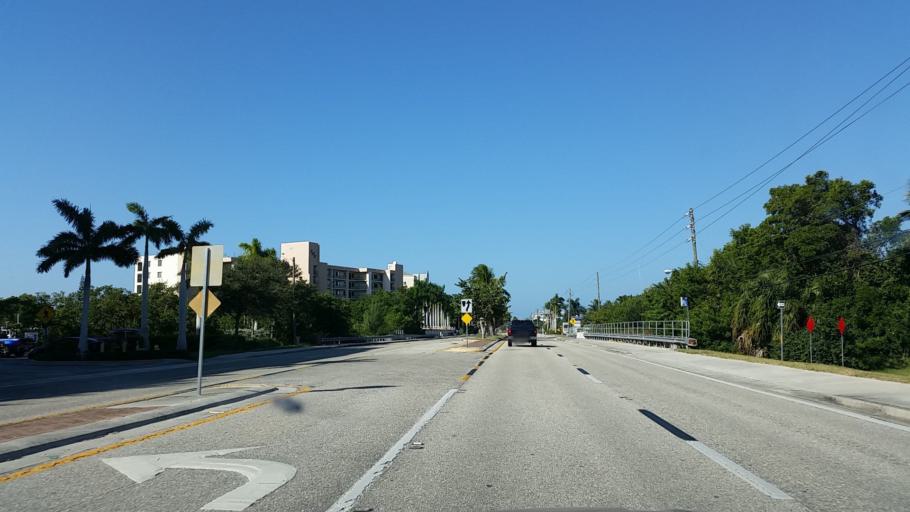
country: US
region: Florida
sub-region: Lee County
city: Bonita Springs
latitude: 26.3305
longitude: -81.8305
